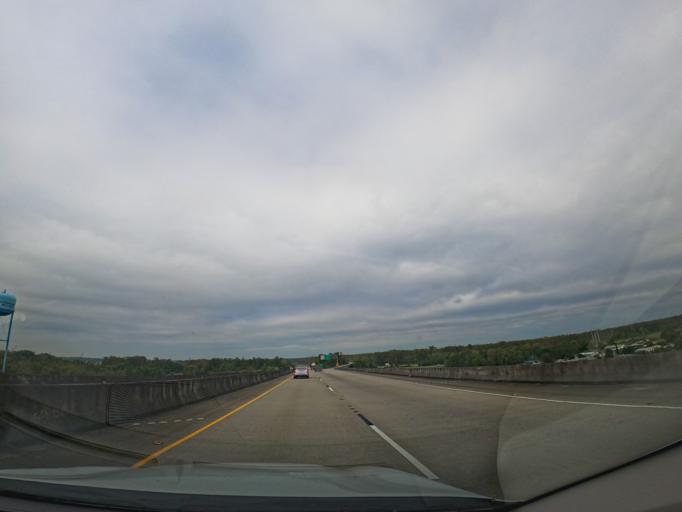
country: US
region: Louisiana
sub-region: Saint Mary Parish
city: Amelia
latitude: 29.6709
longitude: -91.1034
